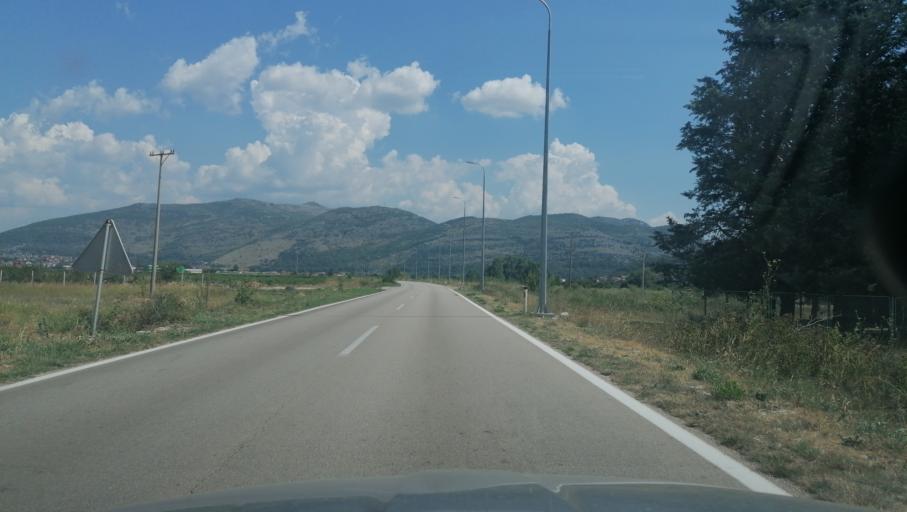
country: BA
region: Republika Srpska
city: Trebinje
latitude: 42.7062
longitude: 18.3182
